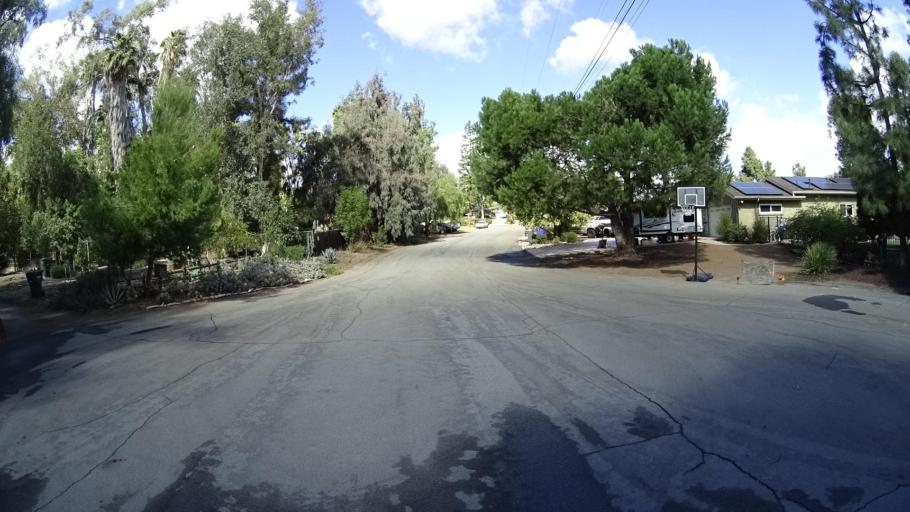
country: US
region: California
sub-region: San Diego County
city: Rancho San Diego
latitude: 32.7591
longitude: -116.9466
